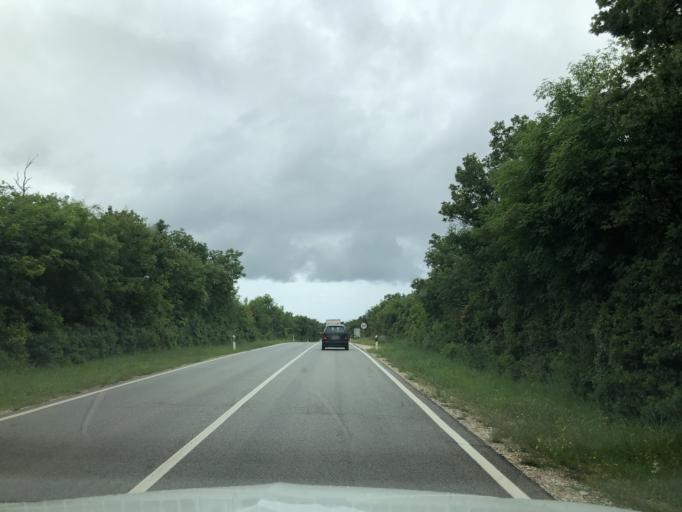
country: SI
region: Piran-Pirano
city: Seca
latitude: 45.4584
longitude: 13.5983
